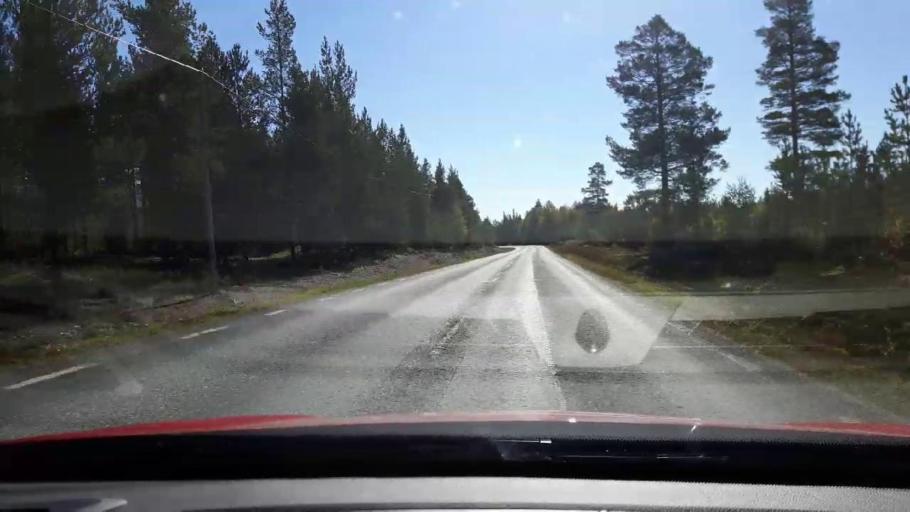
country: SE
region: Jaemtland
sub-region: Harjedalens Kommun
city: Sveg
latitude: 62.4292
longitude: 13.8917
